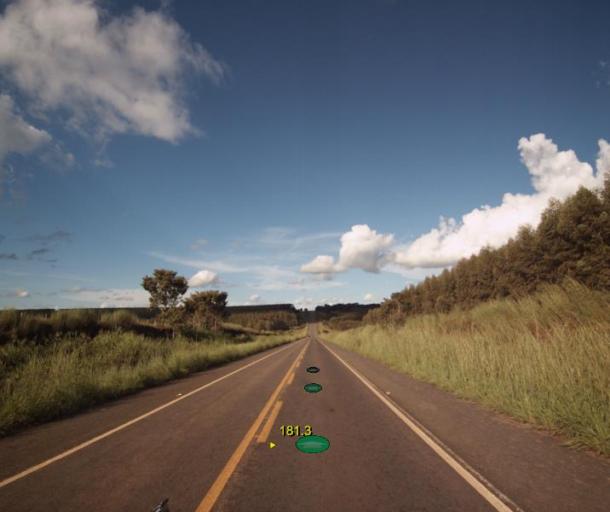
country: BR
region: Goias
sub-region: Itaberai
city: Itaberai
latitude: -15.9891
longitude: -49.7185
